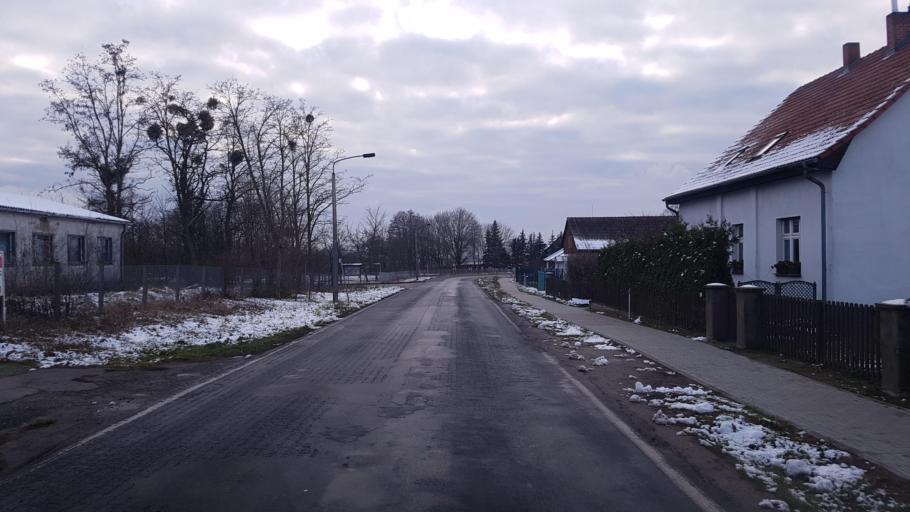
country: DE
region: Brandenburg
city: Rehfelde
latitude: 52.5260
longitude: 13.9218
